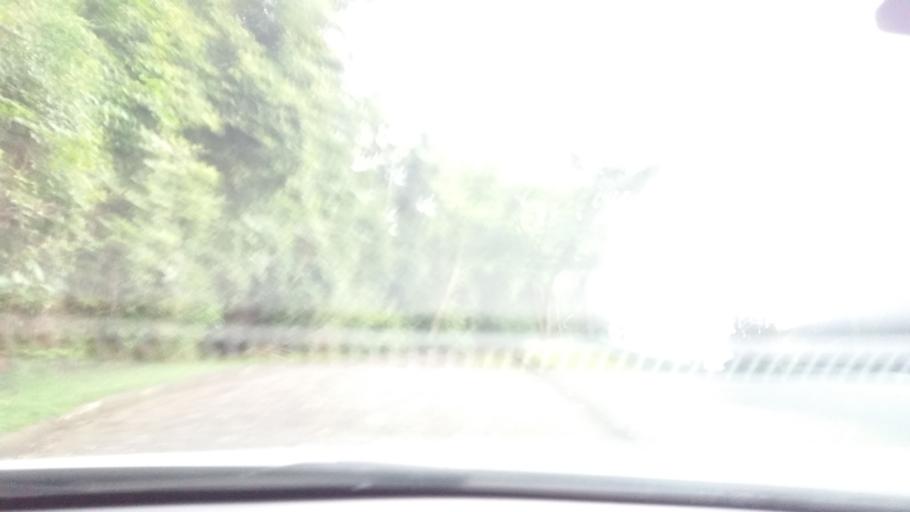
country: BR
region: Sao Paulo
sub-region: Bom Jesus Dos Perdoes
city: Bom Jesus dos Perdoes
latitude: -23.1707
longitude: -46.4617
